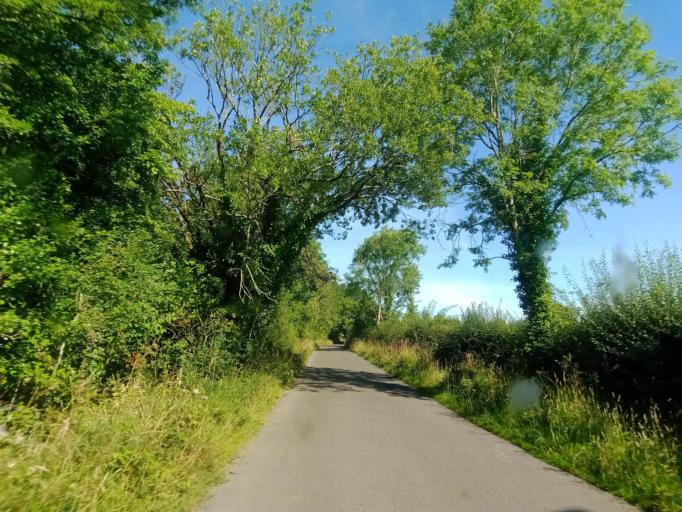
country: IE
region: Leinster
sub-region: Kilkenny
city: Ballyragget
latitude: 52.7764
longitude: -7.4143
